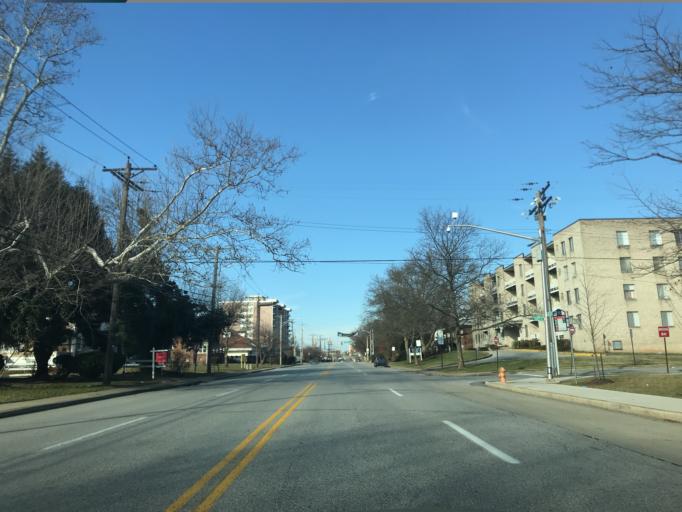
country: US
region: Maryland
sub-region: Baltimore County
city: Lochearn
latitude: 39.3571
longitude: -76.6907
